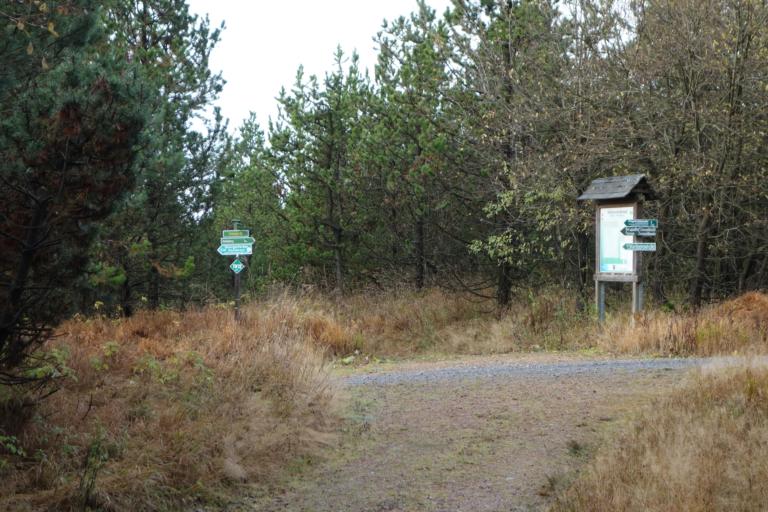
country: DE
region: Saxony
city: Altenberg
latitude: 50.7455
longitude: 13.7393
